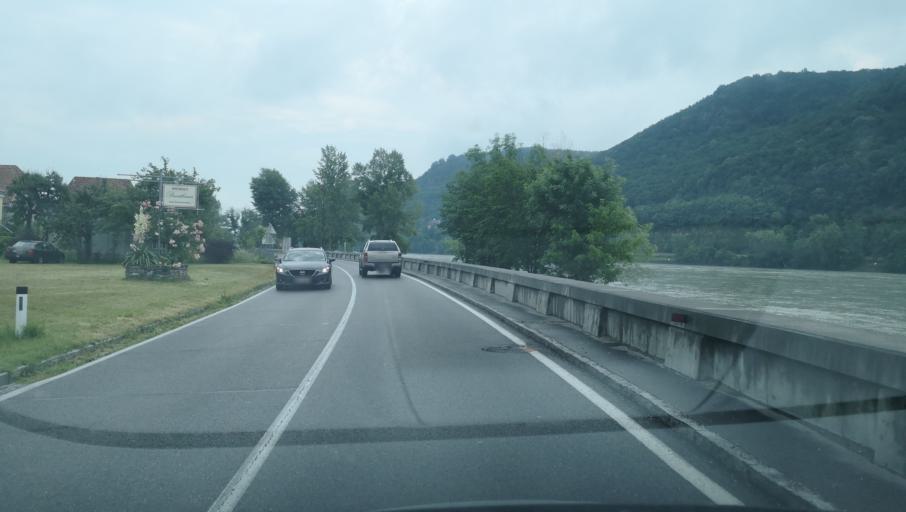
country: AT
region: Lower Austria
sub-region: Politischer Bezirk Krems
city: Durnstein
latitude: 48.3855
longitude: 15.5341
